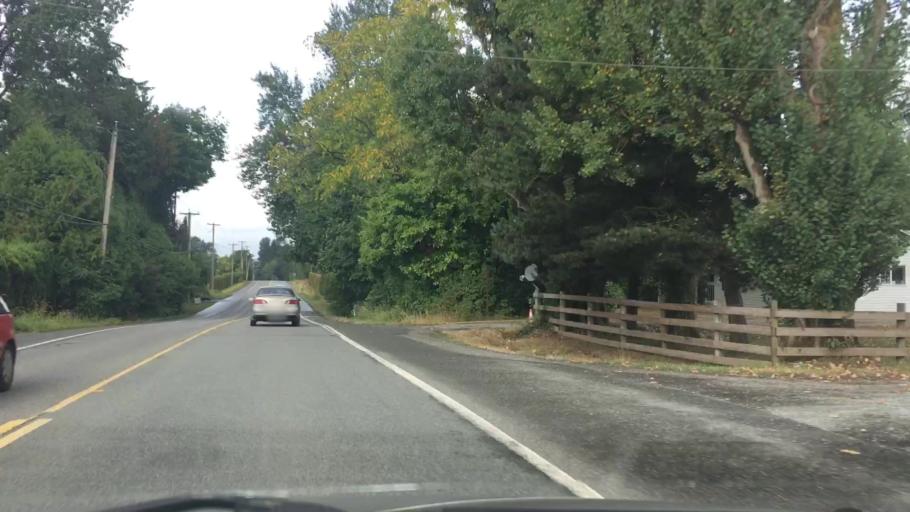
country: CA
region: British Columbia
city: Langley
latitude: 49.1045
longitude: -122.5981
